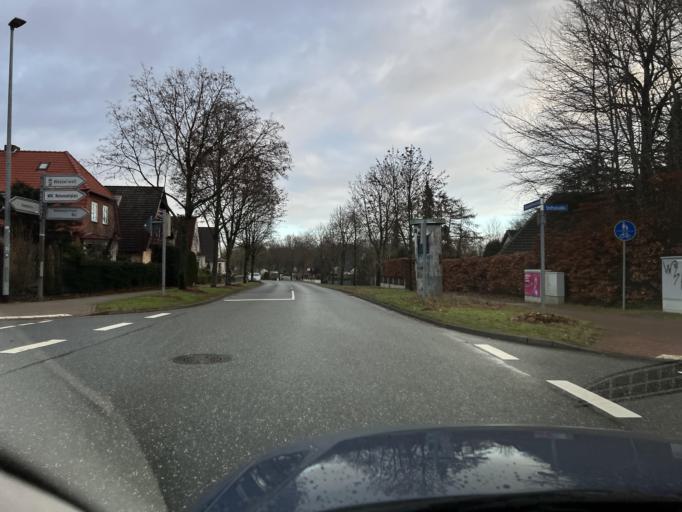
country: DE
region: Schleswig-Holstein
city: Heide
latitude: 54.2041
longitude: 9.1058
